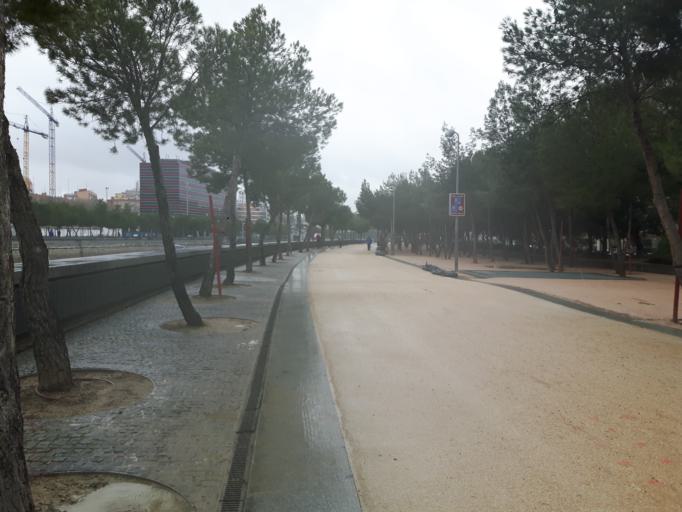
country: ES
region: Madrid
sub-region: Provincia de Madrid
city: Carabanchel
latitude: 40.4087
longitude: -3.7221
